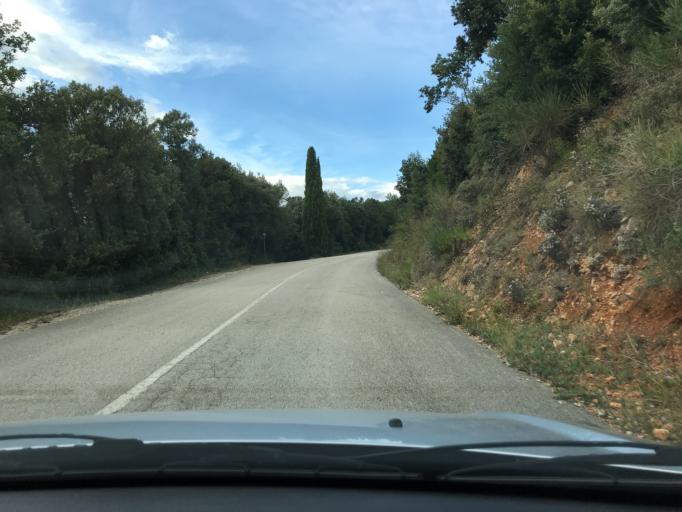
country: IT
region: Umbria
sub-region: Provincia di Terni
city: Montecchio
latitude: 42.6749
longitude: 12.2953
